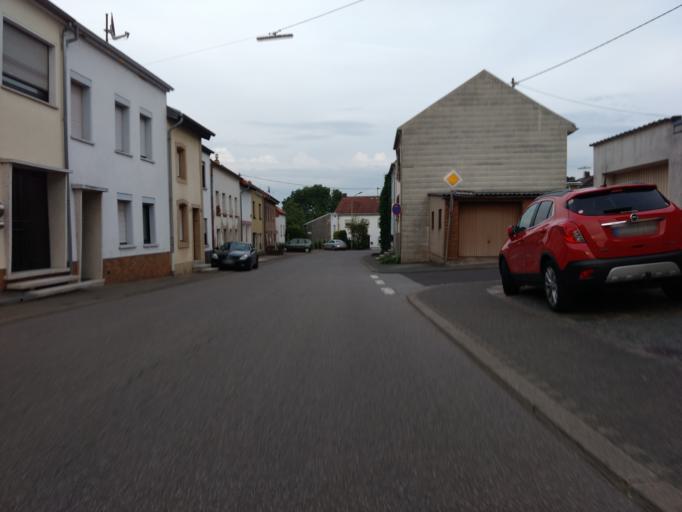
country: DE
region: Saarland
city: Wallerfangen
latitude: 49.3313
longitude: 6.6862
